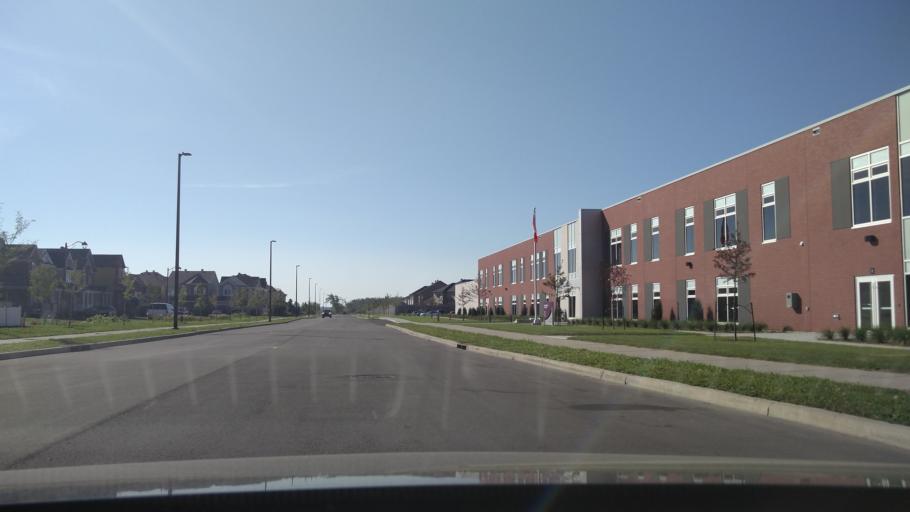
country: CA
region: Ontario
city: Clarence-Rockland
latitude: 45.4514
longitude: -75.4632
